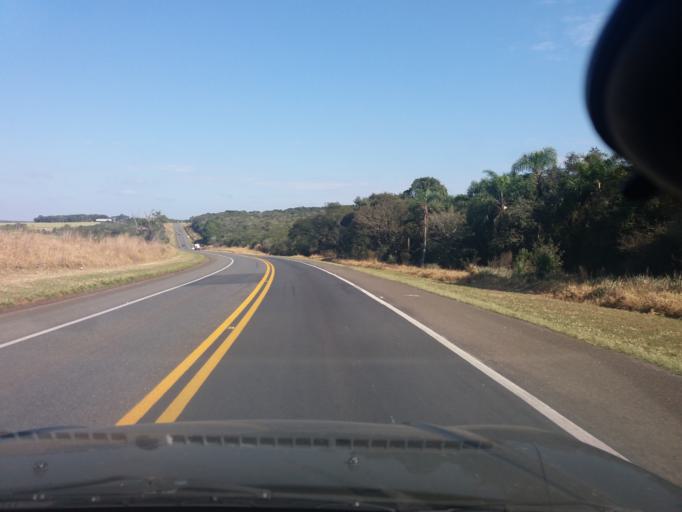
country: BR
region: Sao Paulo
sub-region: Capao Bonito
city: Capao Bonito
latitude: -23.9575
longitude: -48.4645
